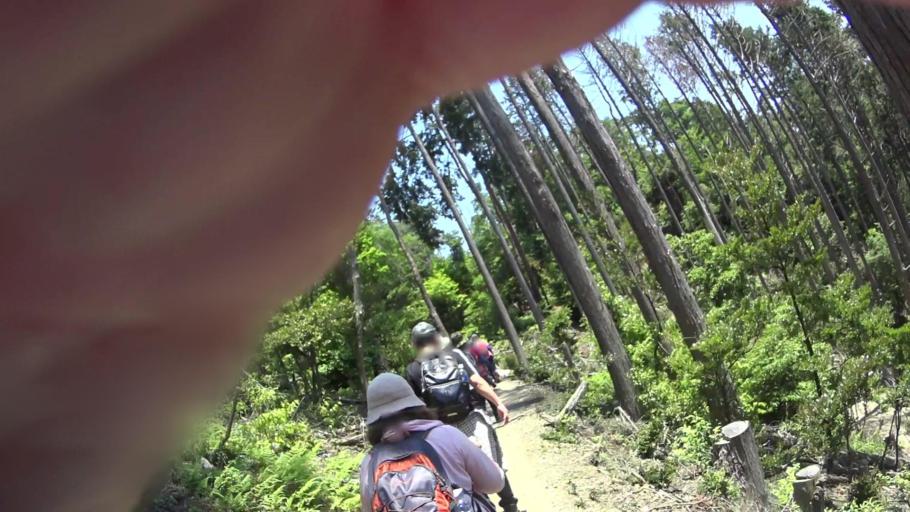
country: JP
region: Kyoto
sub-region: Kyoto-shi
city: Kamigyo-ku
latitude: 35.0178
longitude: 135.8117
